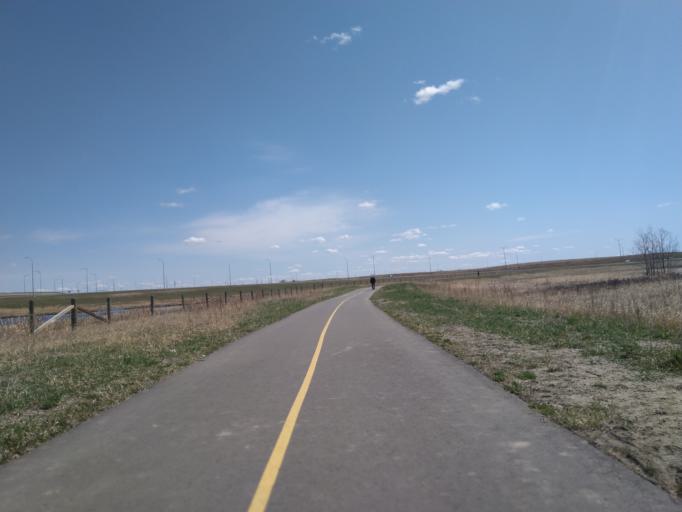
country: CA
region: Alberta
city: Chestermere
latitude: 51.0365
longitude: -113.9264
